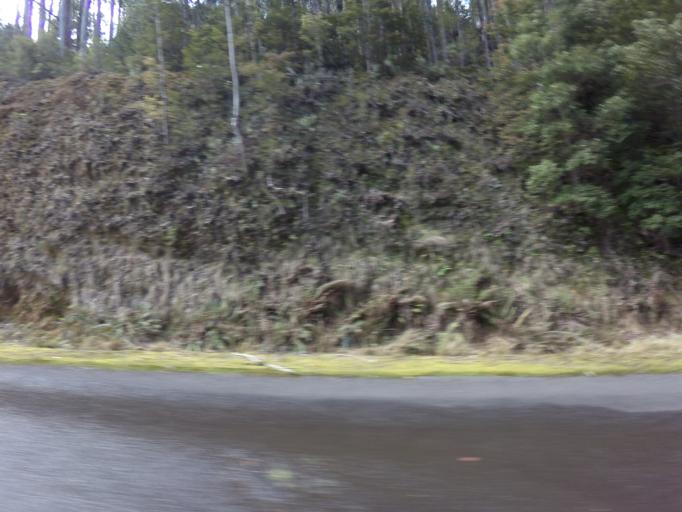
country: AU
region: Tasmania
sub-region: Huon Valley
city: Geeveston
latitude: -42.8184
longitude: 146.3445
